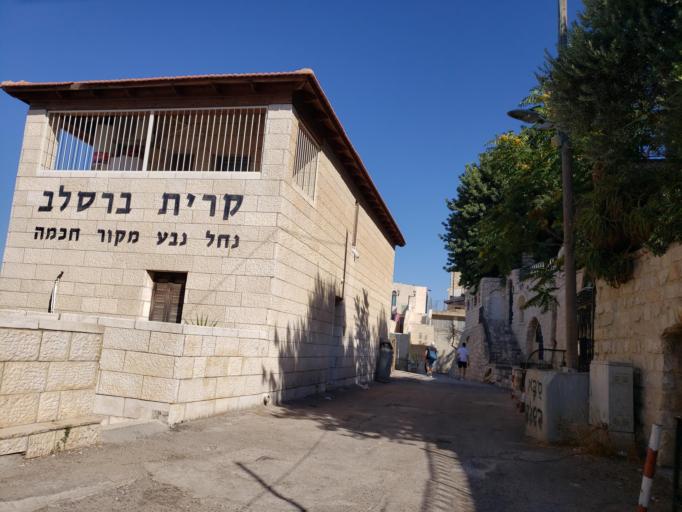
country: IL
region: Northern District
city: Safed
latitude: 32.9679
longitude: 35.4913
